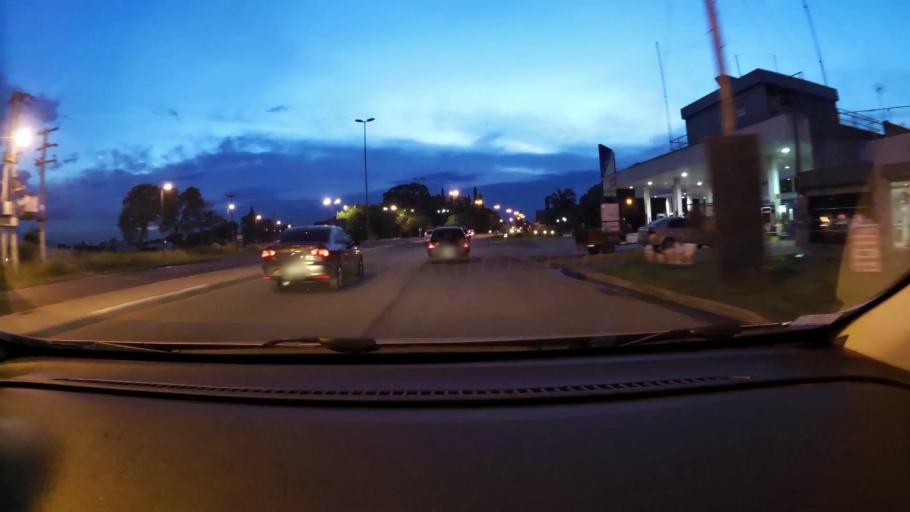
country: AR
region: Buenos Aires
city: San Nicolas de los Arroyos
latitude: -33.3509
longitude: -60.2370
